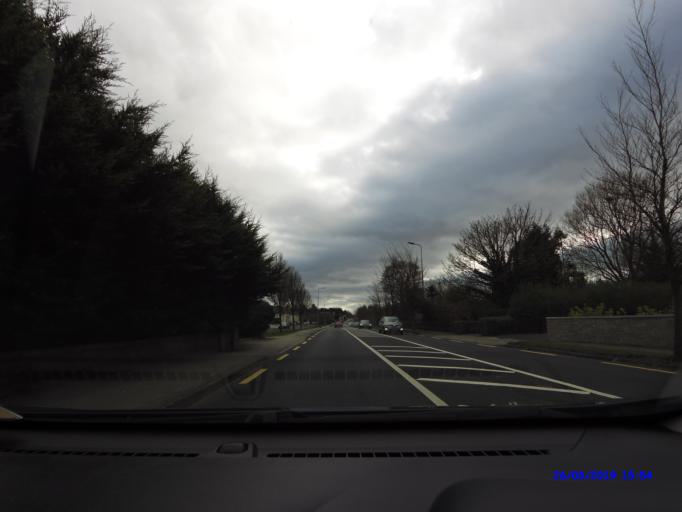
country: IE
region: Connaught
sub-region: Maigh Eo
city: Ballina
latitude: 54.1041
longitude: -9.1637
